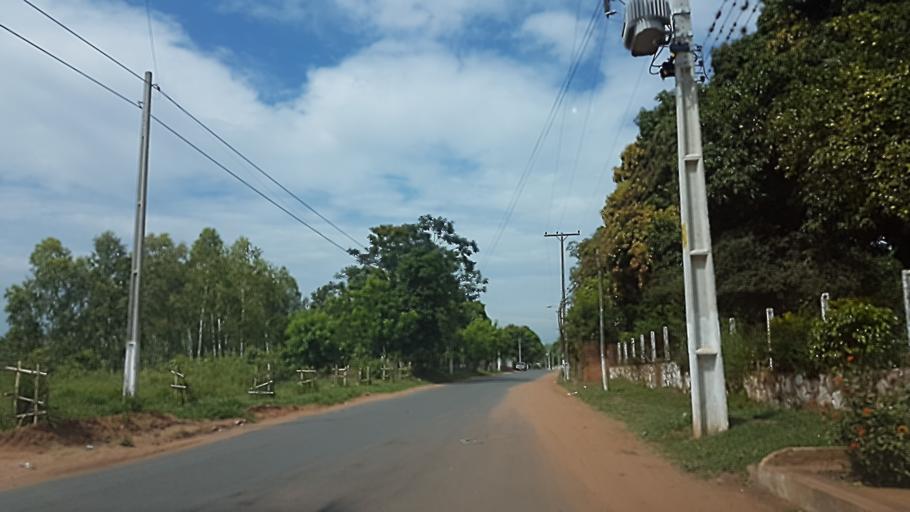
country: PY
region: Central
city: Capiata
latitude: -25.3463
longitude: -57.4304
